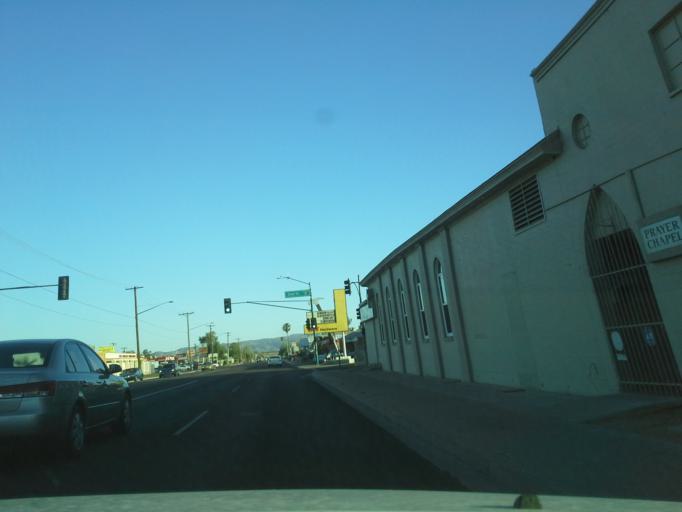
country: US
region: Arizona
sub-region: Maricopa County
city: Phoenix
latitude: 33.4736
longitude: -112.0303
